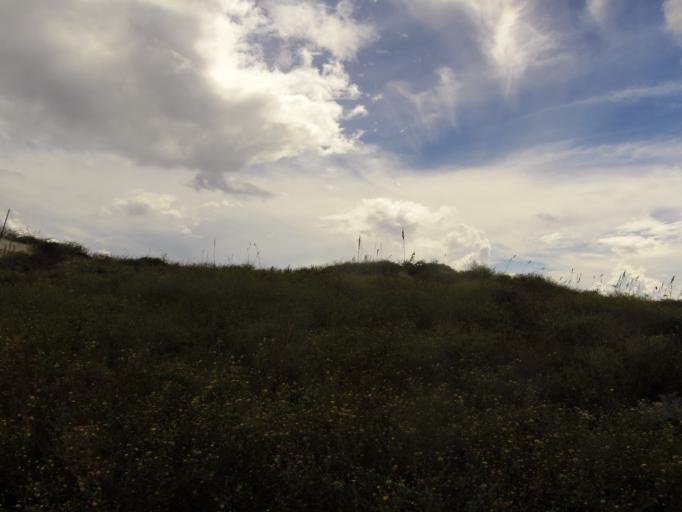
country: US
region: Florida
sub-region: Nassau County
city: Fernandina Beach
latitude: 30.5761
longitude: -81.4443
